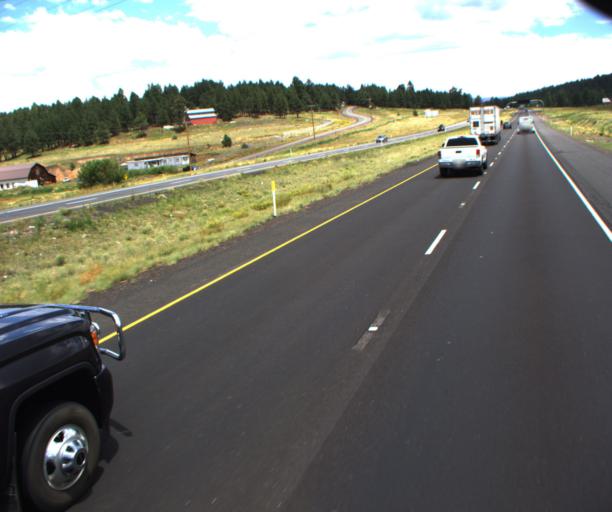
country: US
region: Arizona
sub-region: Coconino County
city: Kachina Village
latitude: 35.0969
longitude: -111.6835
